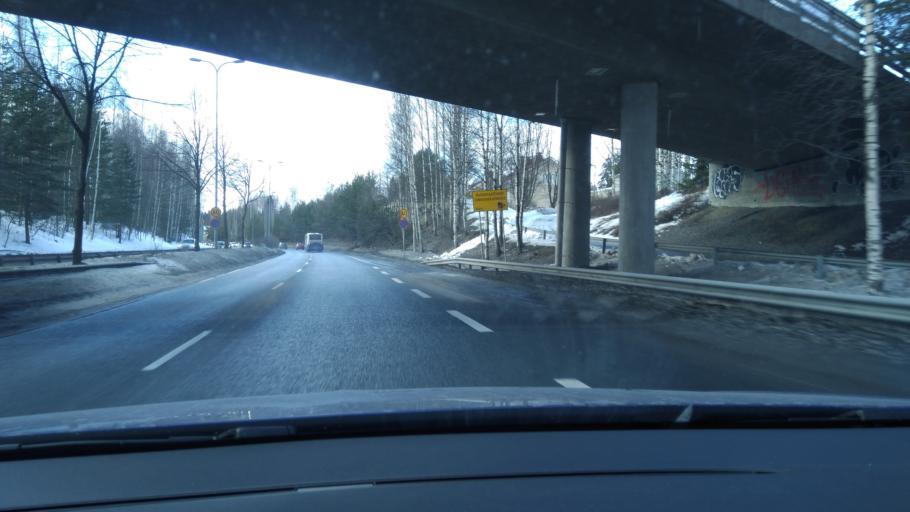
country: FI
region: Pirkanmaa
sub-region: Tampere
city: Tampere
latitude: 61.5040
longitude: 23.8022
